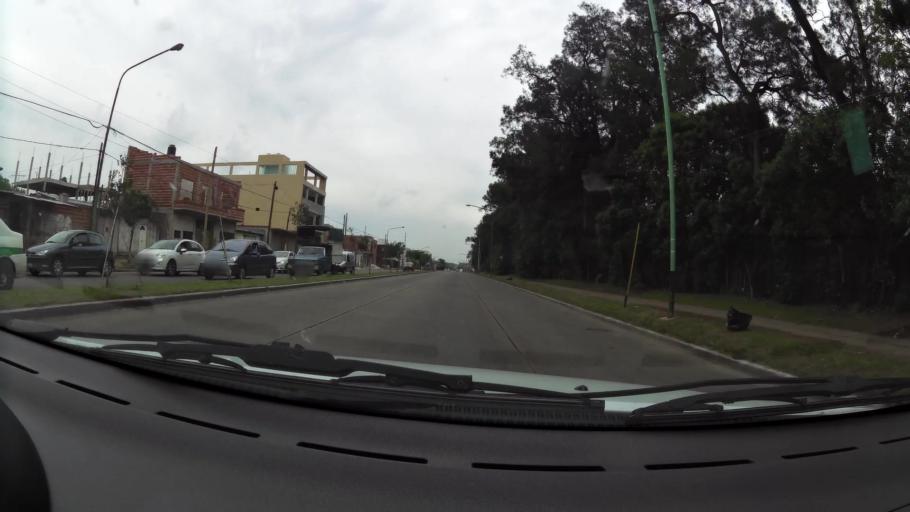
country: AR
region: Buenos Aires
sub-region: Partido de La Plata
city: La Plata
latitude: -34.9082
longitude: -57.9859
